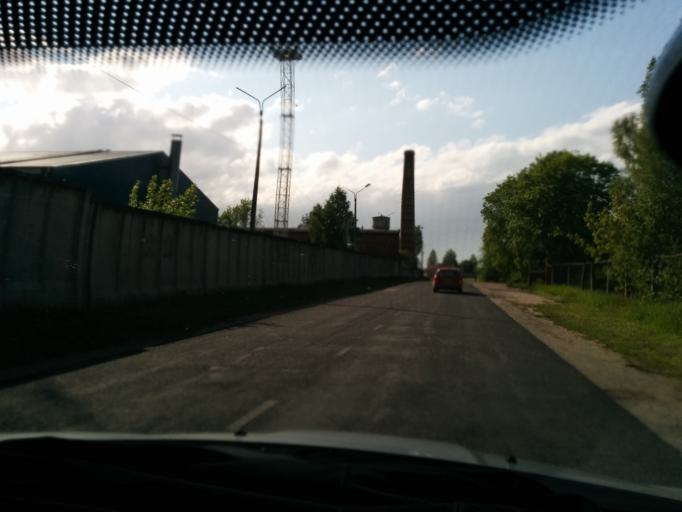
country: EE
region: Harju
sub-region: Loksa linn
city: Loksa
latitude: 59.5857
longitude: 25.7106
